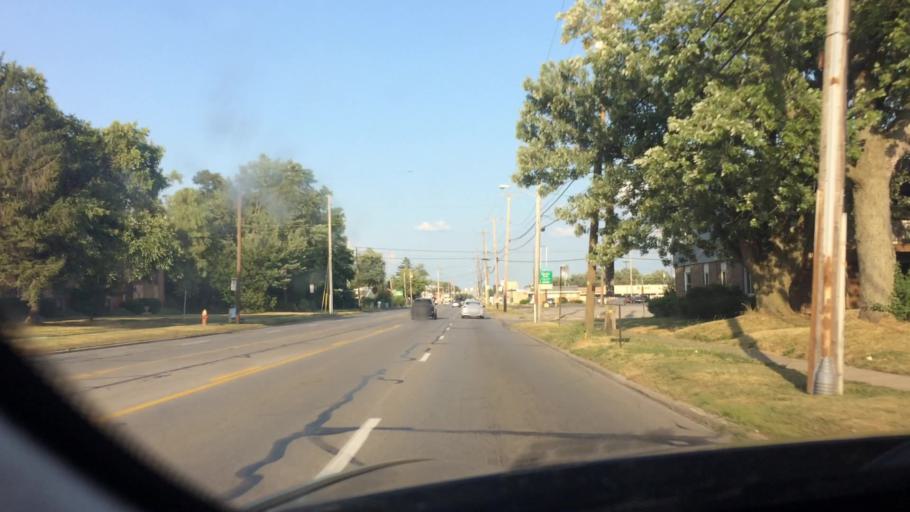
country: US
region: Ohio
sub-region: Lucas County
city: Ottawa Hills
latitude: 41.6535
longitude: -83.6708
